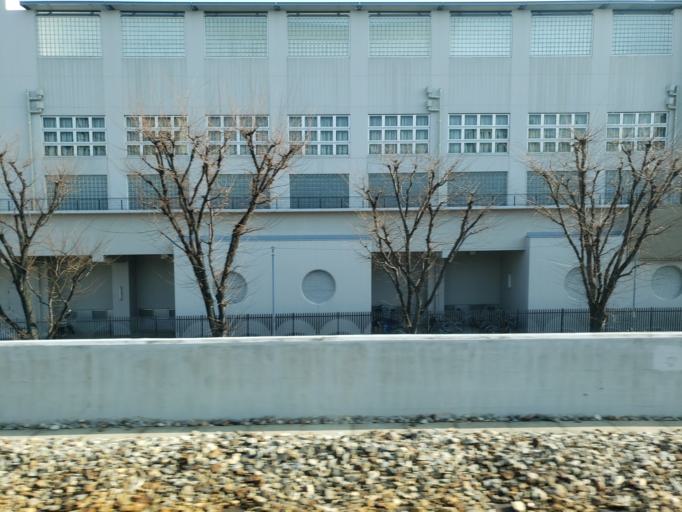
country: JP
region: Hyogo
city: Kobe
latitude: 34.6617
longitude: 135.1532
